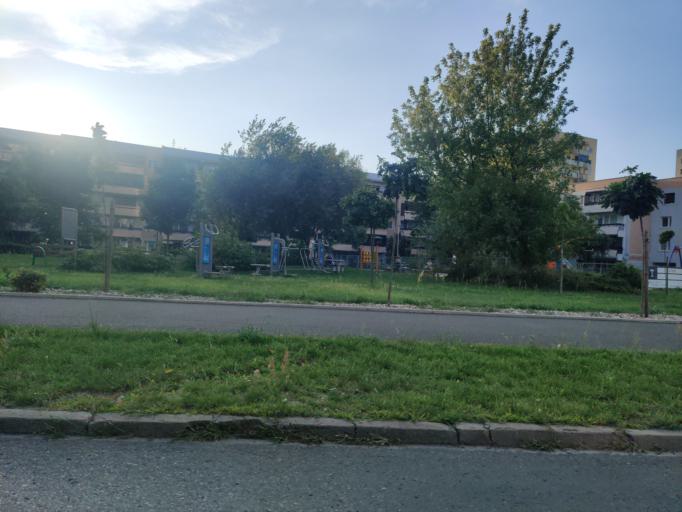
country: PL
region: Greater Poland Voivodeship
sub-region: Konin
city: Konin
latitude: 52.2324
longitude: 18.2597
